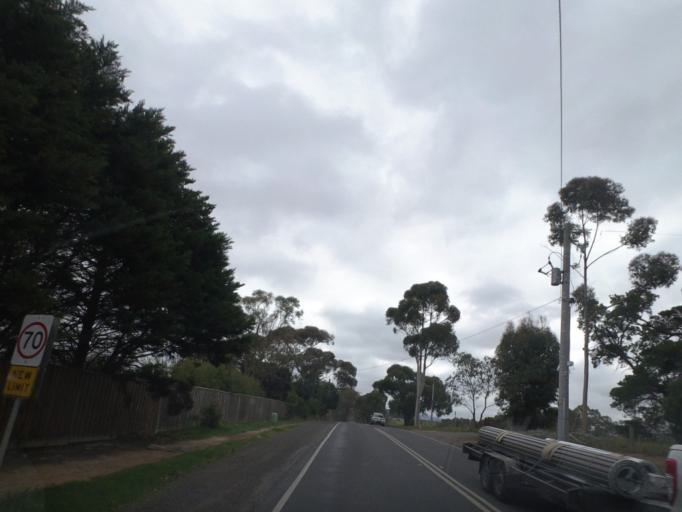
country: AU
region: Victoria
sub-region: Nillumbik
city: Doreen
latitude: -37.6092
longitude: 145.1375
